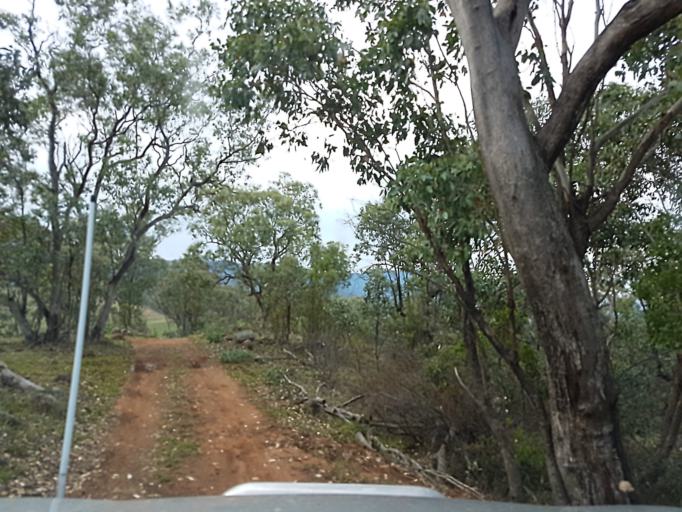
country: AU
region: New South Wales
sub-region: Snowy River
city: Jindabyne
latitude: -36.9671
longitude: 148.3849
